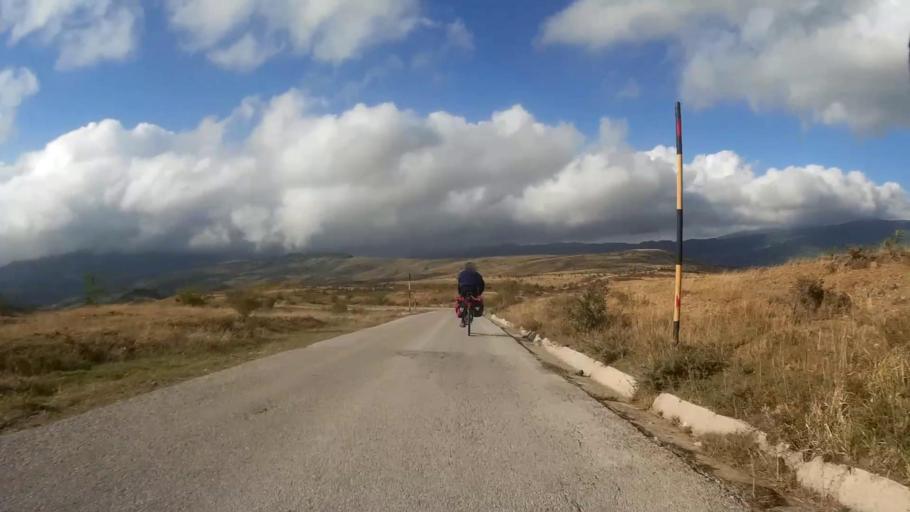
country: IT
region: Basilicate
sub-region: Provincia di Potenza
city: Viggianello
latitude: 39.9599
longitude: 16.1444
